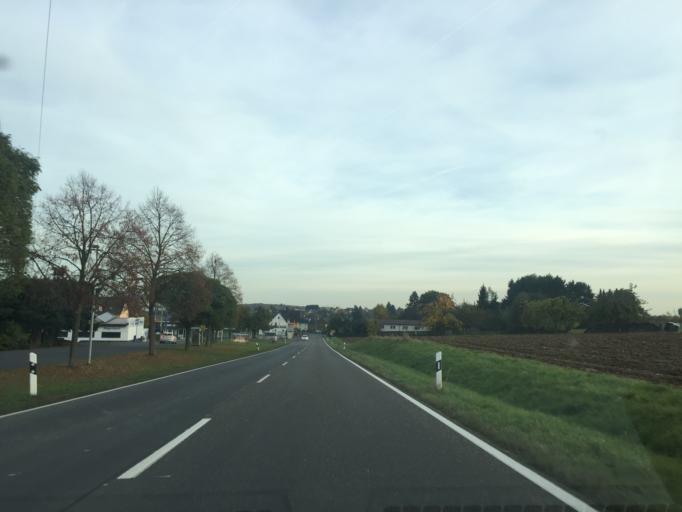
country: DE
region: Rheinland-Pfalz
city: Hundsangen
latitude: 50.4574
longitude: 7.9798
